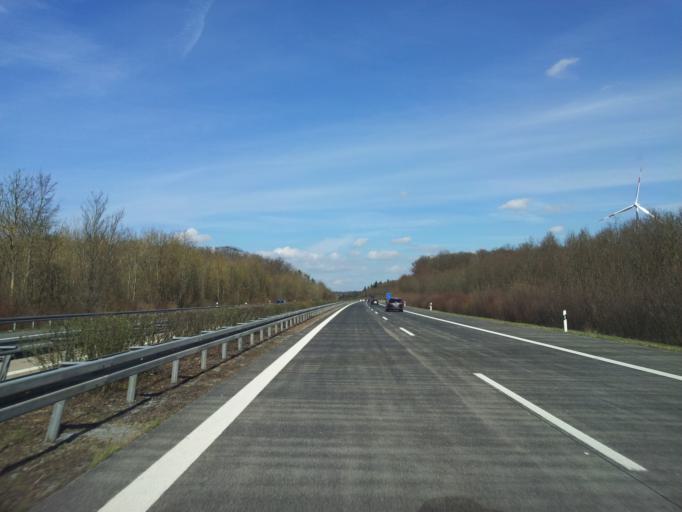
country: DE
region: Baden-Wuerttemberg
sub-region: Regierungsbezirk Stuttgart
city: Buch am Ahorn
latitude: 49.5109
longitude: 9.5658
